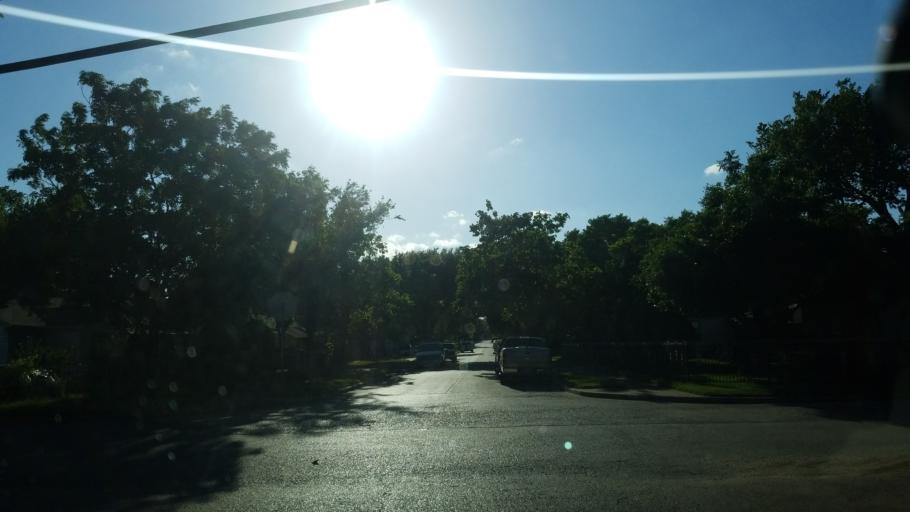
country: US
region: Texas
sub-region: Dallas County
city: Dallas
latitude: 32.7767
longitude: -96.7090
